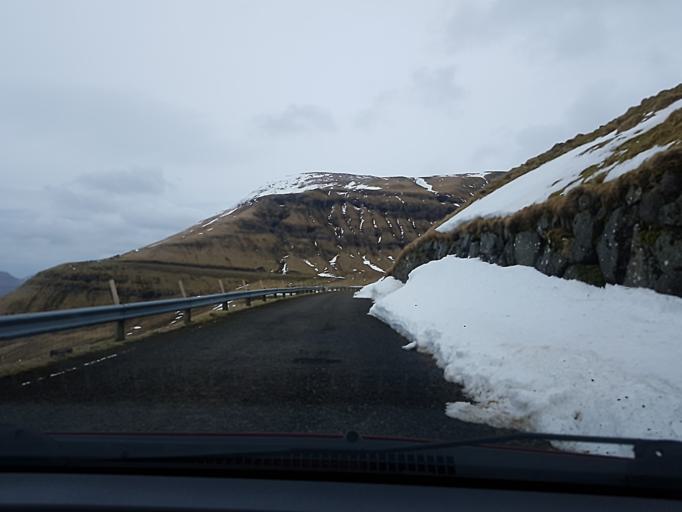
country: FO
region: Streymoy
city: Hoyvik
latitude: 61.9948
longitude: -6.8865
